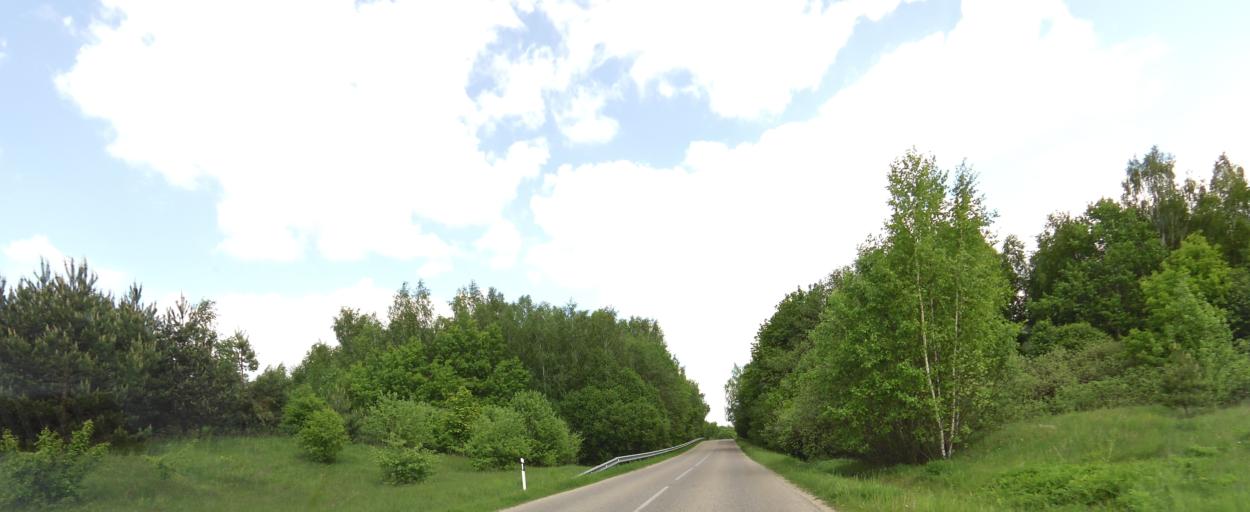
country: LT
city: Trakai
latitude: 54.6747
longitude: 24.9437
